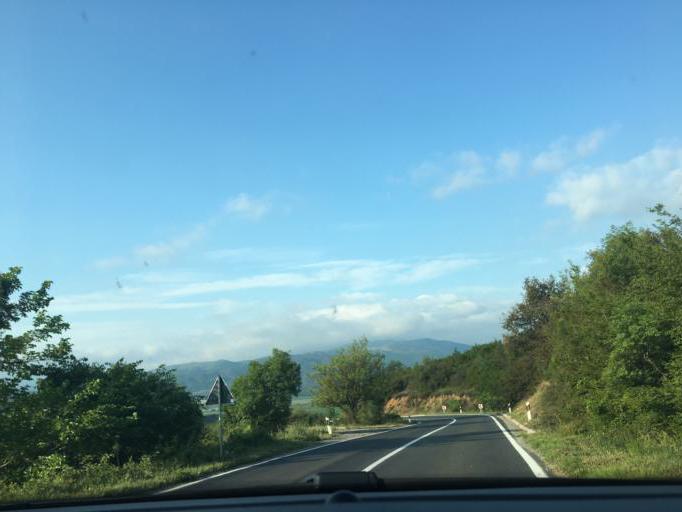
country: MK
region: Valandovo
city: Valandovo
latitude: 41.3208
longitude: 22.5980
